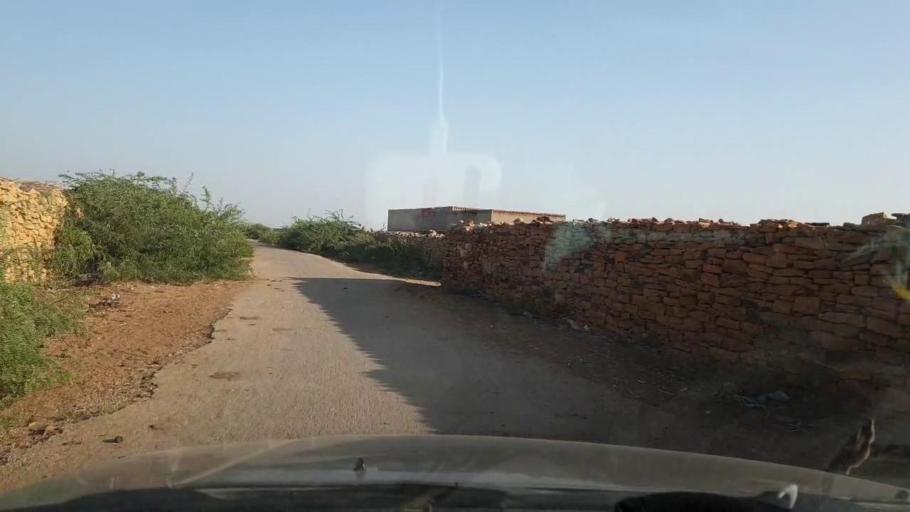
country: PK
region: Sindh
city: Kotri
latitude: 25.1329
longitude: 68.2293
